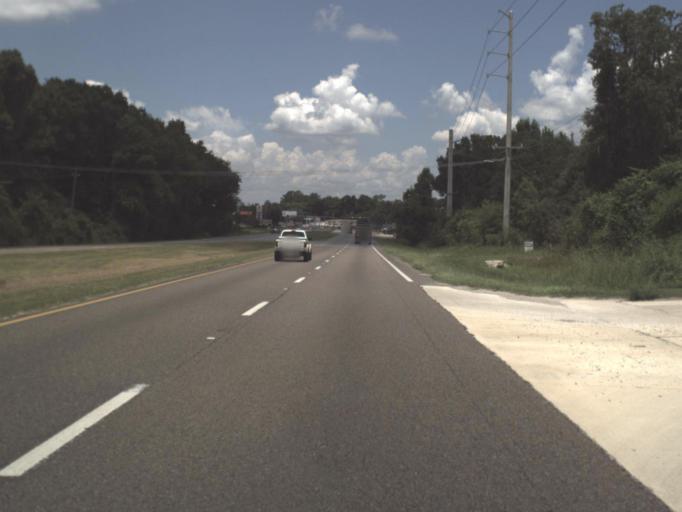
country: US
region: Florida
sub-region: Putnam County
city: East Palatka
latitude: 29.6434
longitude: -81.5926
